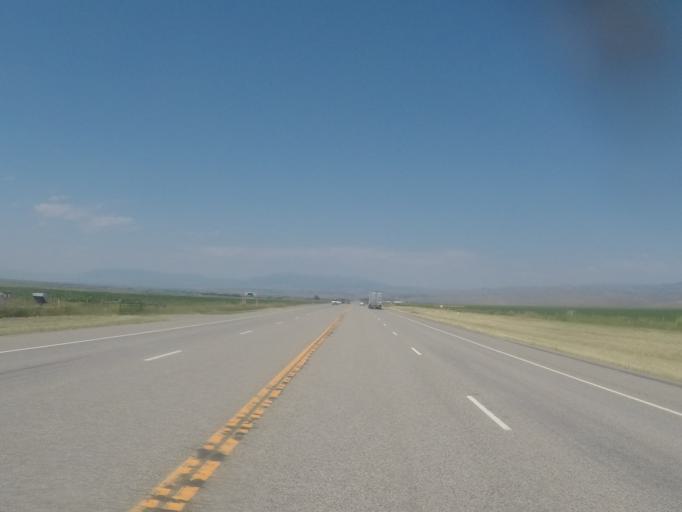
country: US
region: Montana
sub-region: Broadwater County
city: Townsend
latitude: 46.1136
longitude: -111.5046
